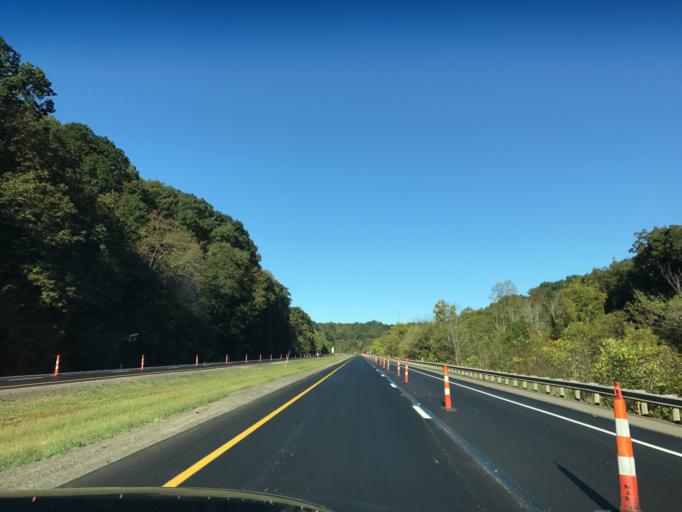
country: US
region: Ohio
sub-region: Washington County
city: Reno
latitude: 39.2450
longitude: -81.3724
